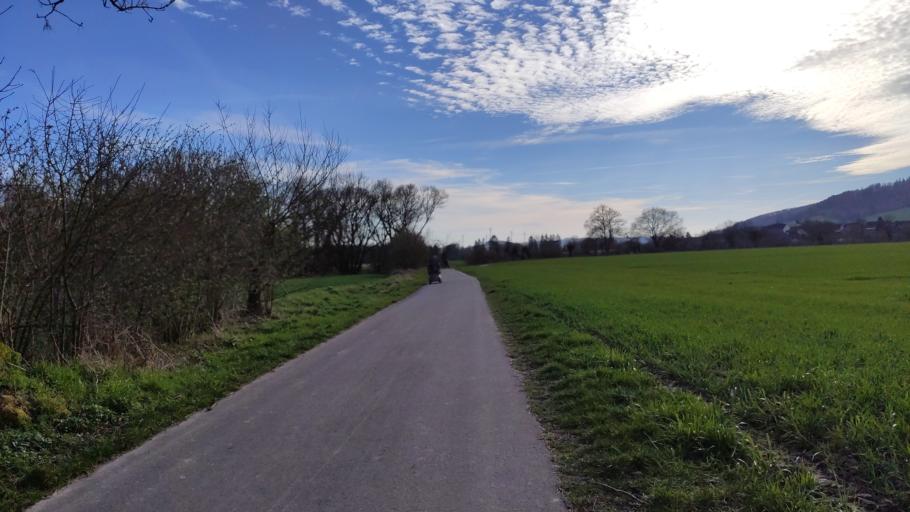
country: DE
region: Lower Saxony
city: Boffzen
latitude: 51.7366
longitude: 9.3732
